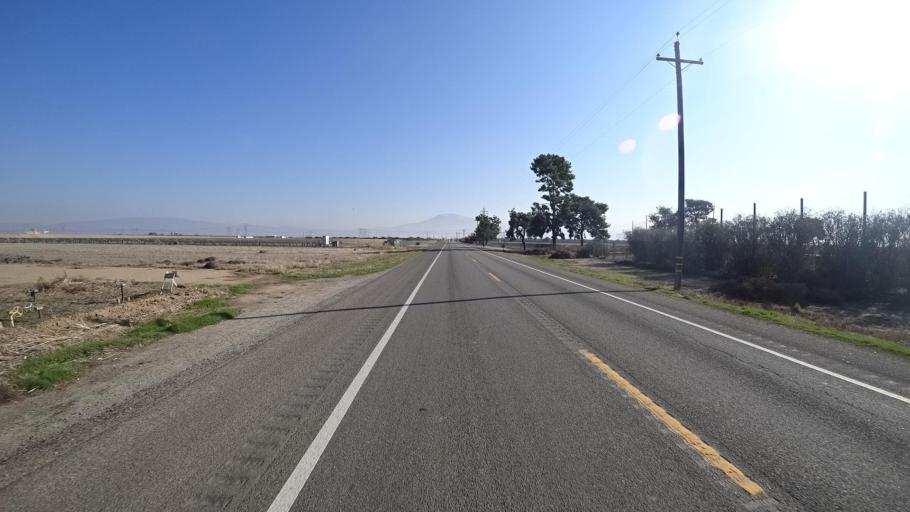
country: US
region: California
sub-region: Kern County
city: Weedpatch
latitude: 35.2087
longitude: -118.9287
